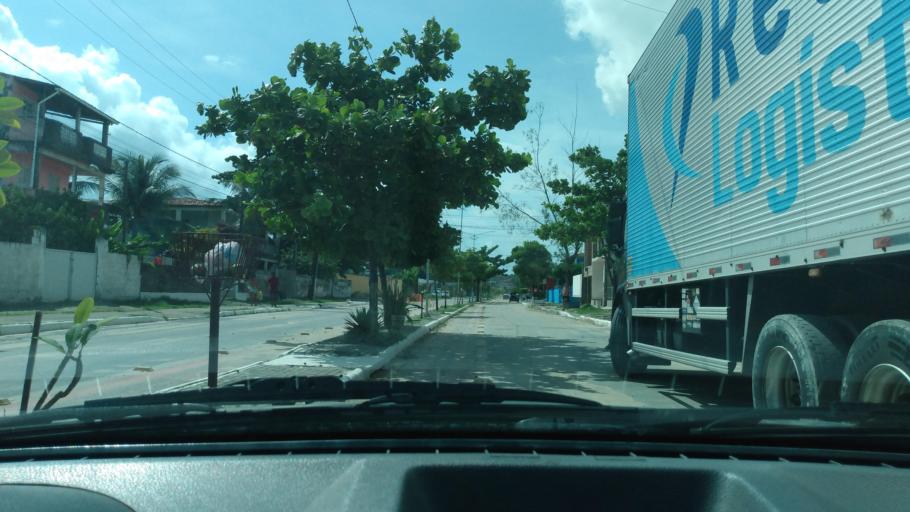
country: BR
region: Pernambuco
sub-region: Cabo De Santo Agostinho
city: Cabo
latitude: -8.3286
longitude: -34.9537
